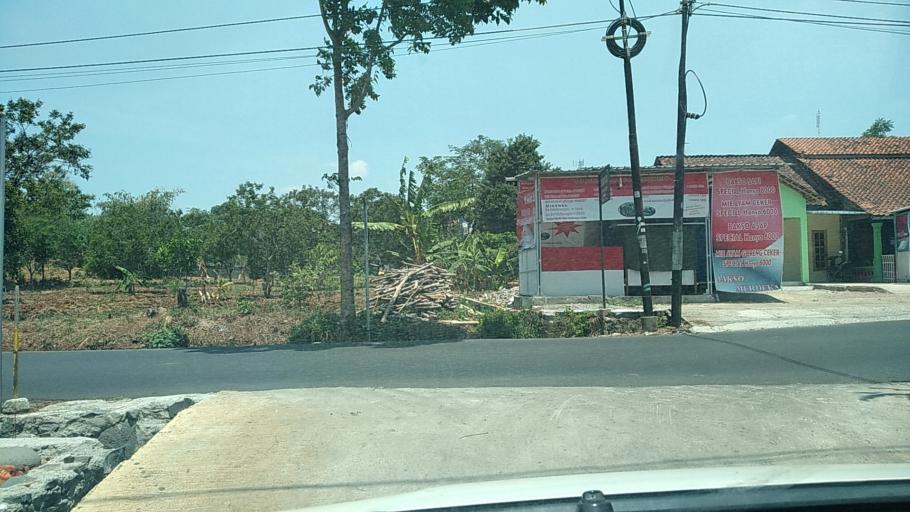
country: ID
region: Central Java
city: Ungaran
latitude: -7.0719
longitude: 110.3861
